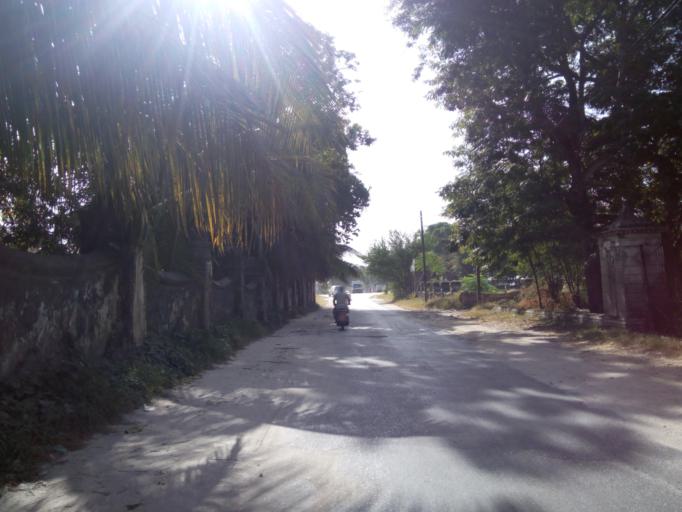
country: TZ
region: Zanzibar Urban/West
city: Zanzibar
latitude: -6.1726
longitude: 39.2000
